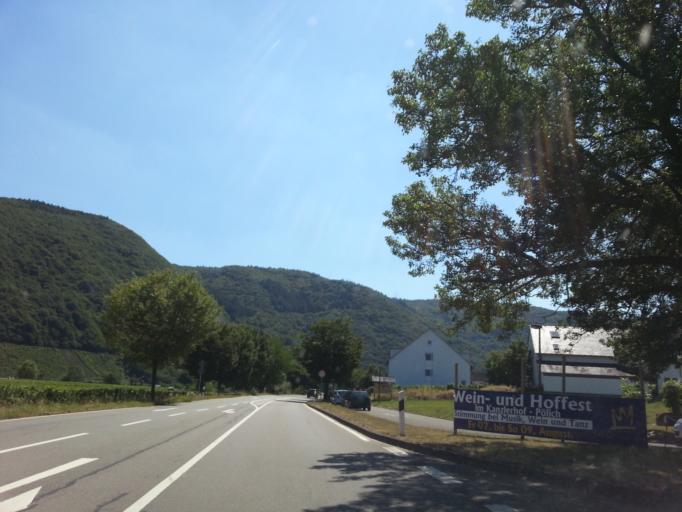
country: DE
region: Rheinland-Pfalz
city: Polich
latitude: 49.8000
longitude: 6.8492
